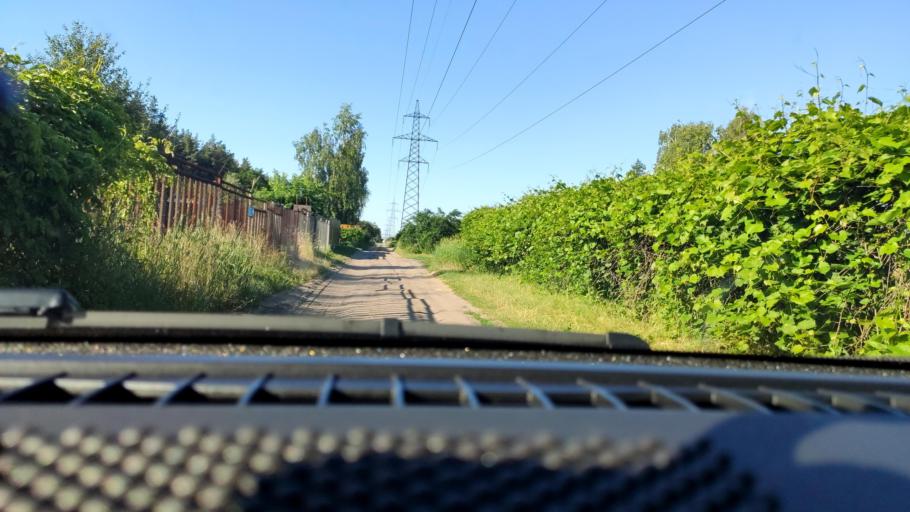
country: RU
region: Voronezj
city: Volya
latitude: 51.7453
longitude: 39.4617
